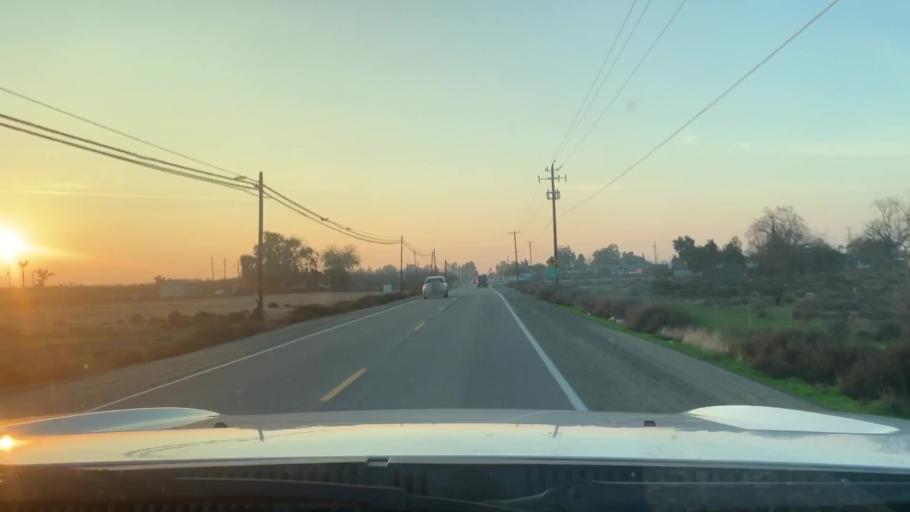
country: US
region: California
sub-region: Kern County
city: Rosedale
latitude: 35.3835
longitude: -119.1963
